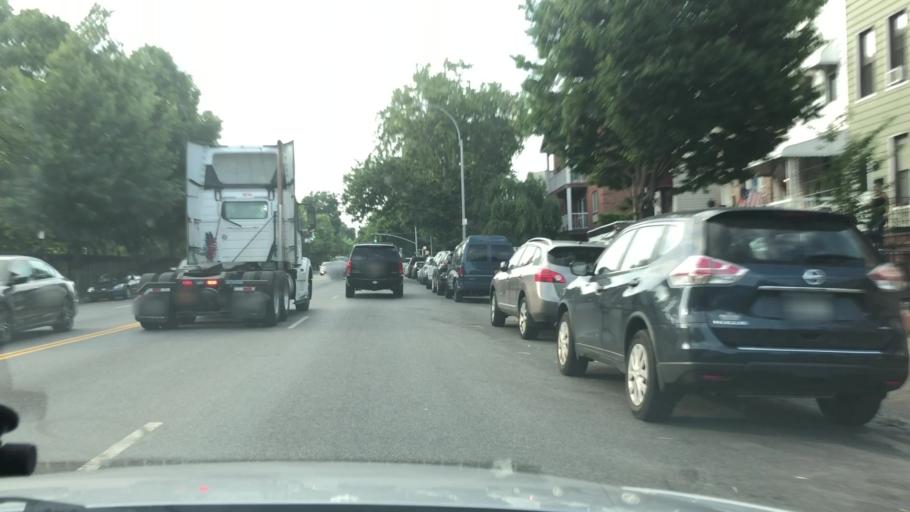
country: US
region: New York
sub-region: Kings County
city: Brooklyn
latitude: 40.6505
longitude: -73.9809
